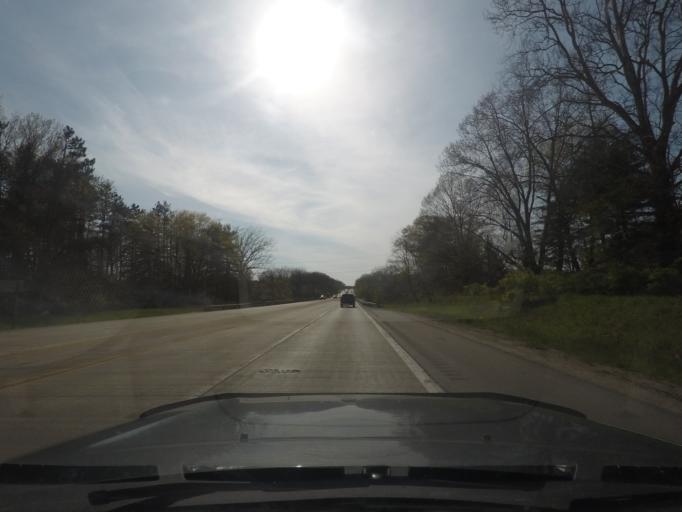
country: US
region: Michigan
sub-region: Berrien County
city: Niles
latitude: 41.8013
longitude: -86.2649
